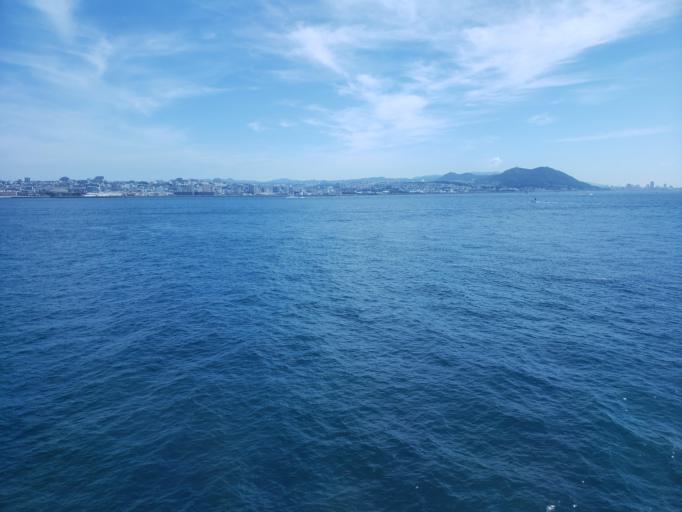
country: JP
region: Hyogo
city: Akashi
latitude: 34.6072
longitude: 135.0448
